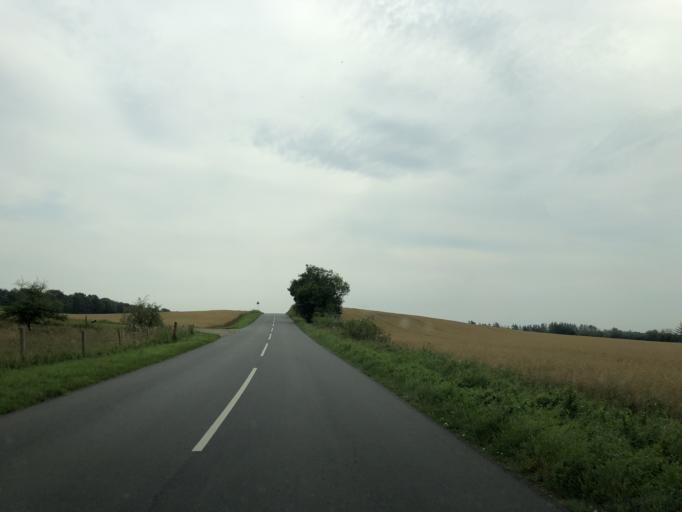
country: DK
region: Central Jutland
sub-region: Viborg Kommune
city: Stoholm
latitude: 56.4520
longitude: 9.1691
